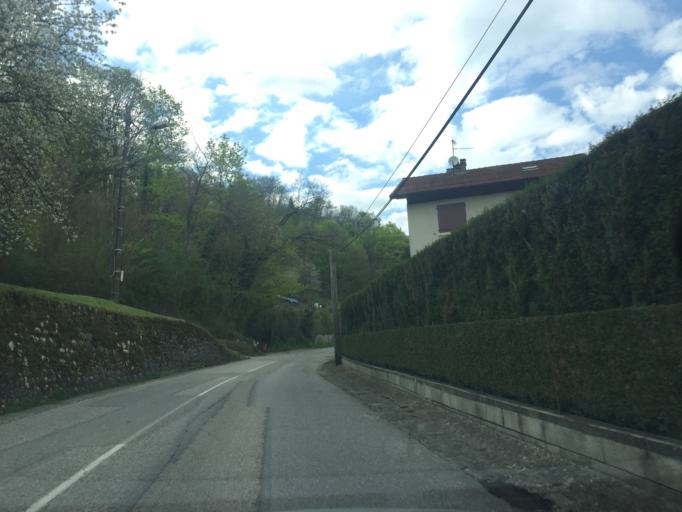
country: FR
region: Rhone-Alpes
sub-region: Departement de la Savoie
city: Cognin
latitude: 45.5660
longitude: 5.8871
